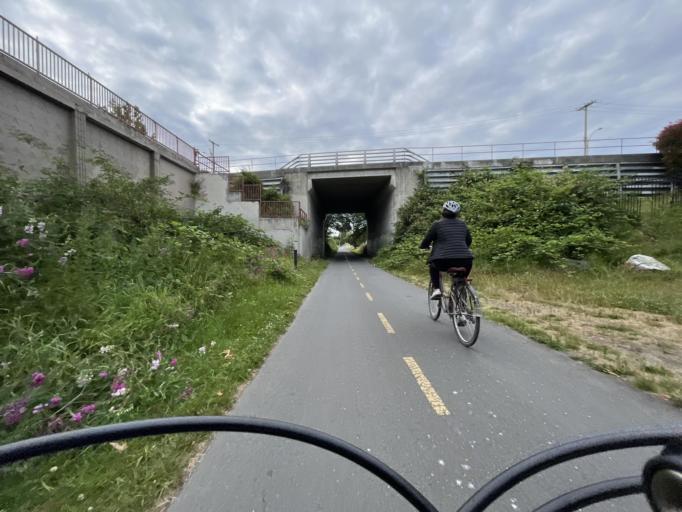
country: CA
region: British Columbia
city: Victoria
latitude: 48.4523
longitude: -123.3765
